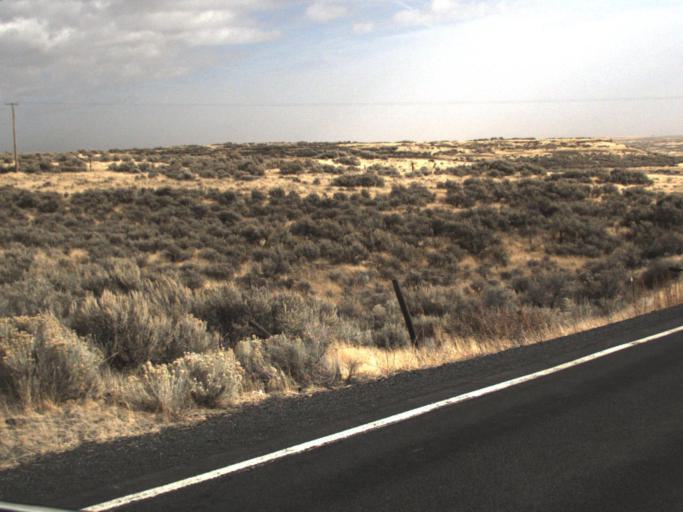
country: US
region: Washington
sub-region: Adams County
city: Ritzville
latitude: 47.4249
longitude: -118.7042
